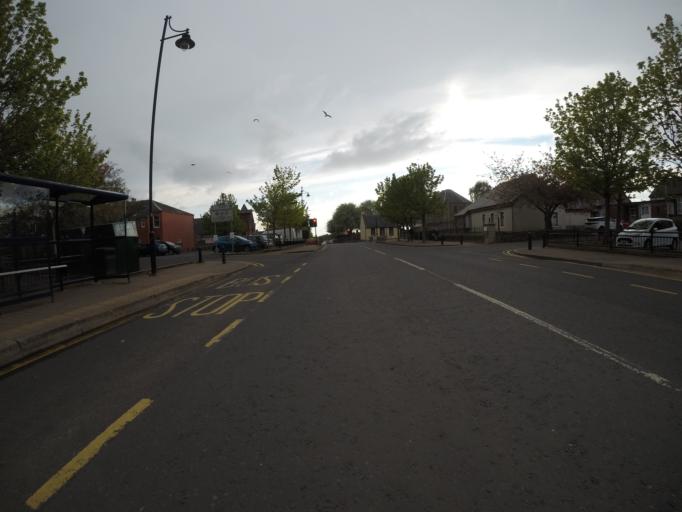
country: GB
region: Scotland
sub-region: North Ayrshire
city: Dreghorn
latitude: 55.6098
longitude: -4.6169
